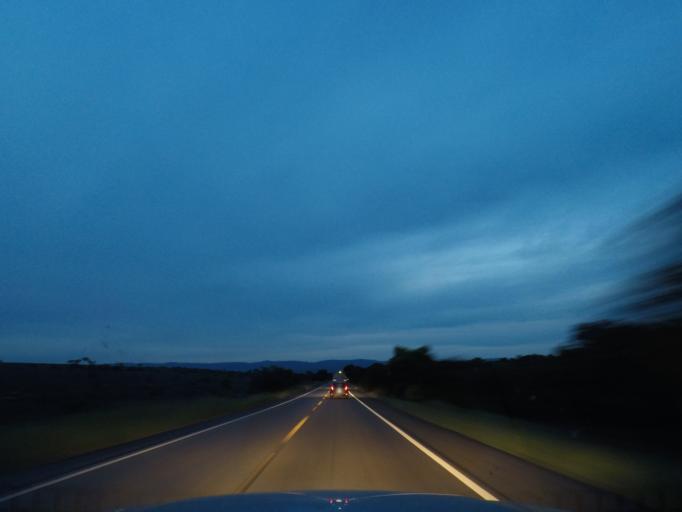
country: BR
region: Bahia
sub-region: Andarai
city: Vera Cruz
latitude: -12.4947
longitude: -41.3075
